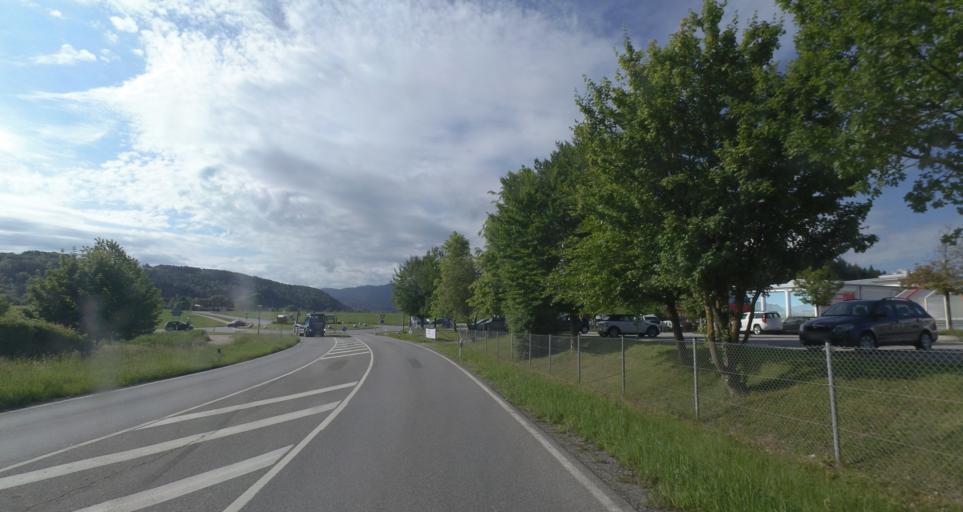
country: DE
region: Bavaria
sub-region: Upper Bavaria
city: Vachendorf
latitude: 47.8544
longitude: 12.6298
